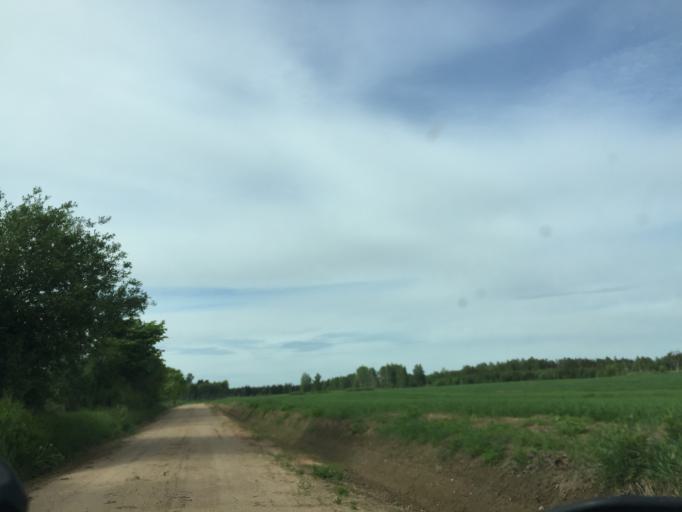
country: LV
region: Beverina
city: Murmuiza
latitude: 57.4651
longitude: 25.4395
